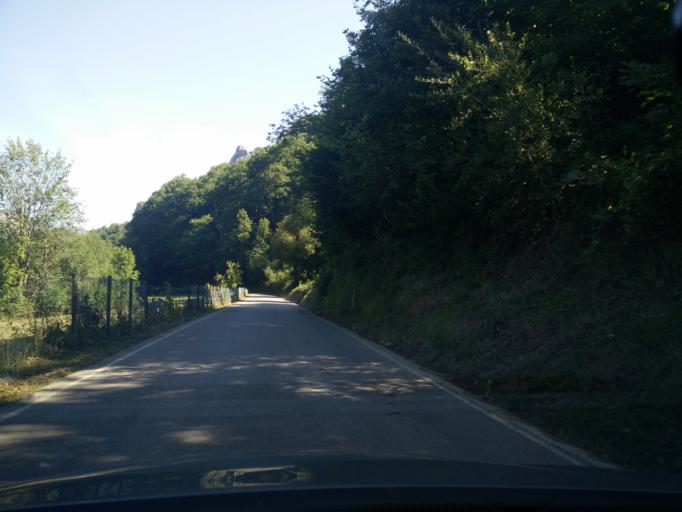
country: ES
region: Asturias
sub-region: Province of Asturias
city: Campo de Caso
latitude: 43.1566
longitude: -5.3926
